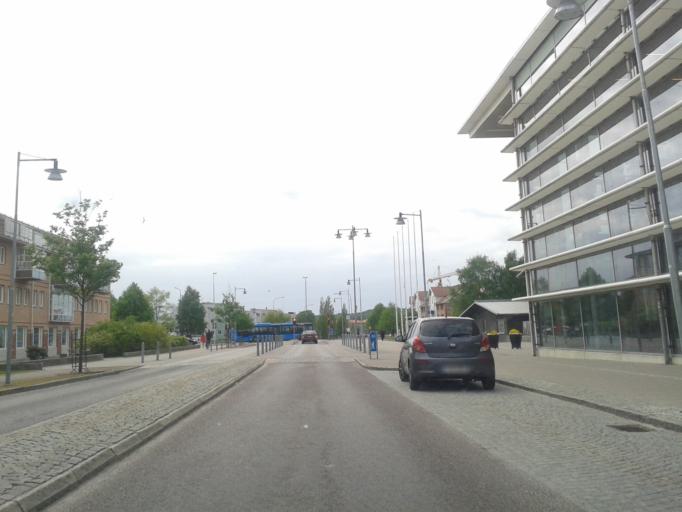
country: SE
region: Vaestra Goetaland
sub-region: Kungalvs Kommun
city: Kungalv
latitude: 57.8747
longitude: 11.9783
